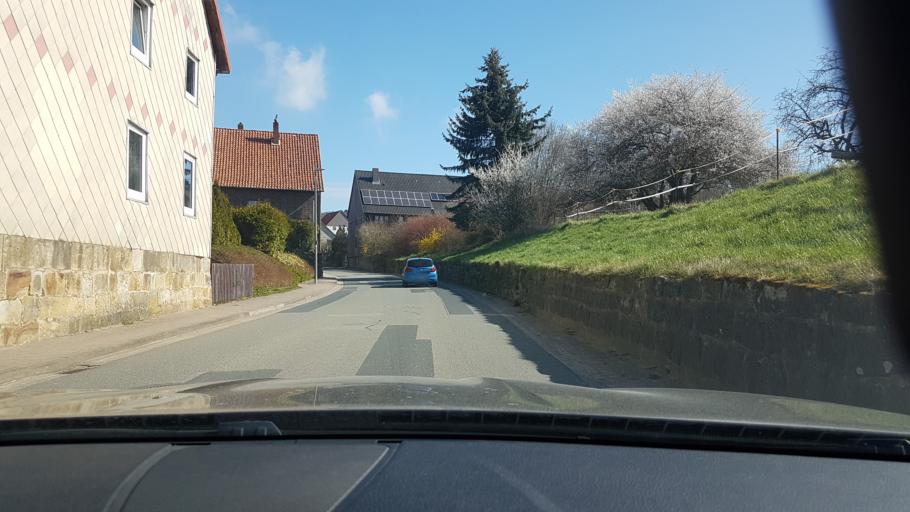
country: DE
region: Lower Saxony
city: Coppenbrugge
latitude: 52.1336
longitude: 9.5641
